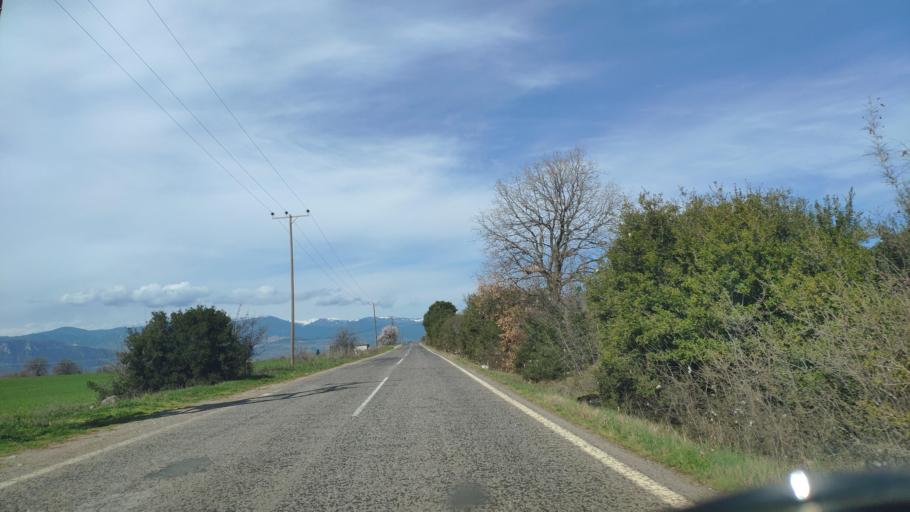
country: GR
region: Central Greece
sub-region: Nomos Fthiotidos
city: Amfikleia
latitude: 38.7014
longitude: 22.5124
